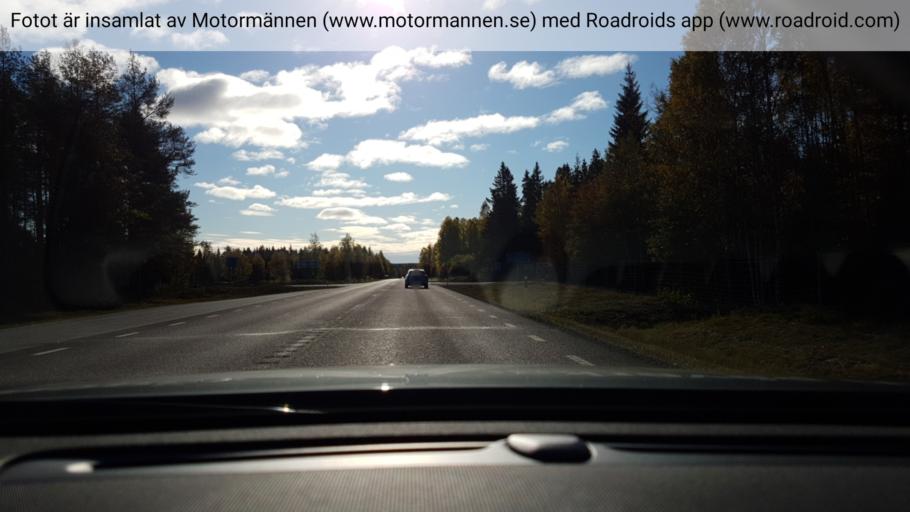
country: SE
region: Vaesterbotten
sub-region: Skelleftea Kommun
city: Burea
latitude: 64.4135
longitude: 21.2921
